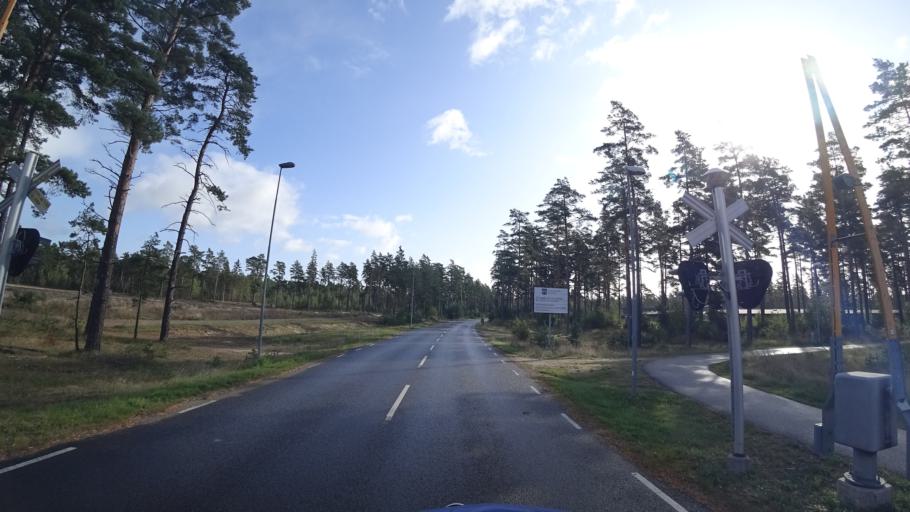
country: SE
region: Skane
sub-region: Kristianstads Kommun
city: Ahus
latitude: 55.9503
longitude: 14.2861
